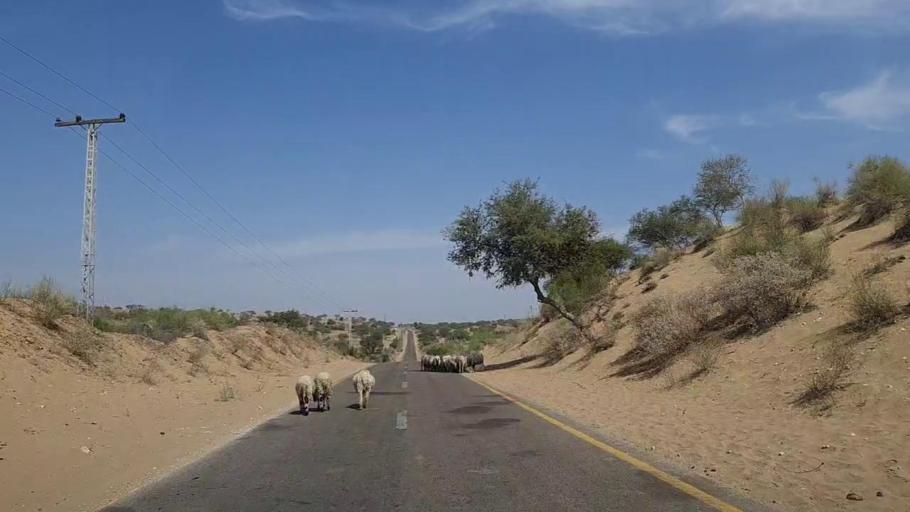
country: PK
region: Sindh
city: Mithi
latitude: 24.8347
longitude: 69.8323
